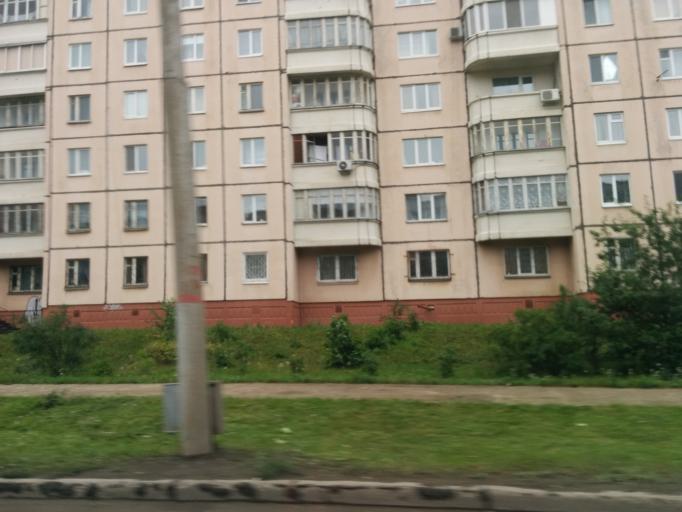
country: RU
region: Perm
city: Kondratovo
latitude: 57.9953
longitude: 56.1361
